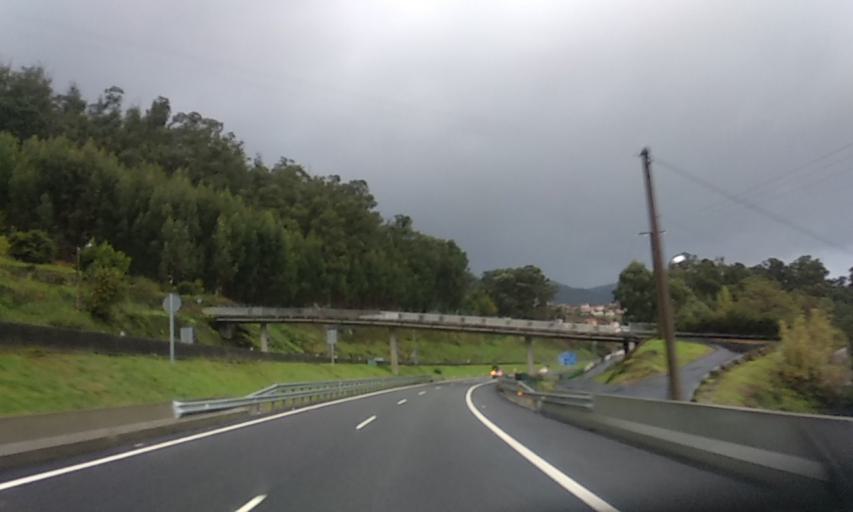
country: ES
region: Galicia
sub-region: Provincia de Pontevedra
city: Redondela
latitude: 42.3081
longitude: -8.6652
